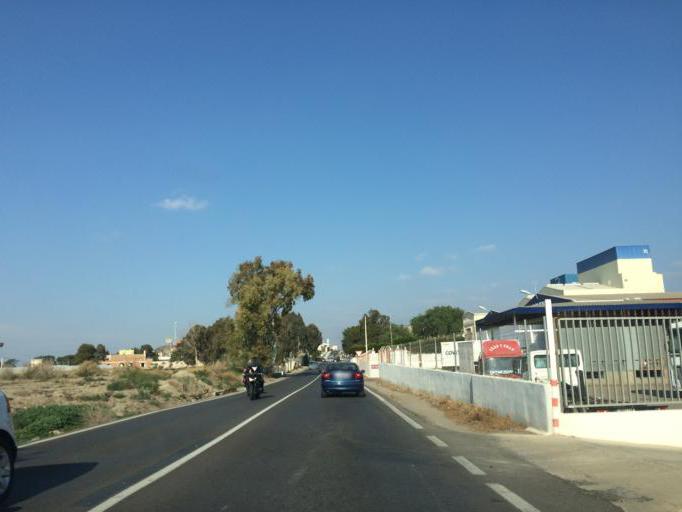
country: ES
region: Andalusia
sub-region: Provincia de Almeria
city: Huercal de Almeria
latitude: 36.8513
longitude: -2.4207
